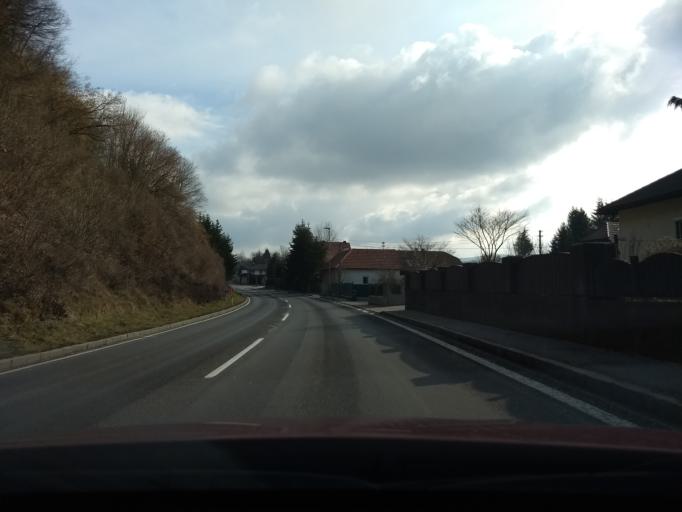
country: AT
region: Upper Austria
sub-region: Politischer Bezirk Steyr-Land
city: Garsten
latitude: 48.0466
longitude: 14.3730
